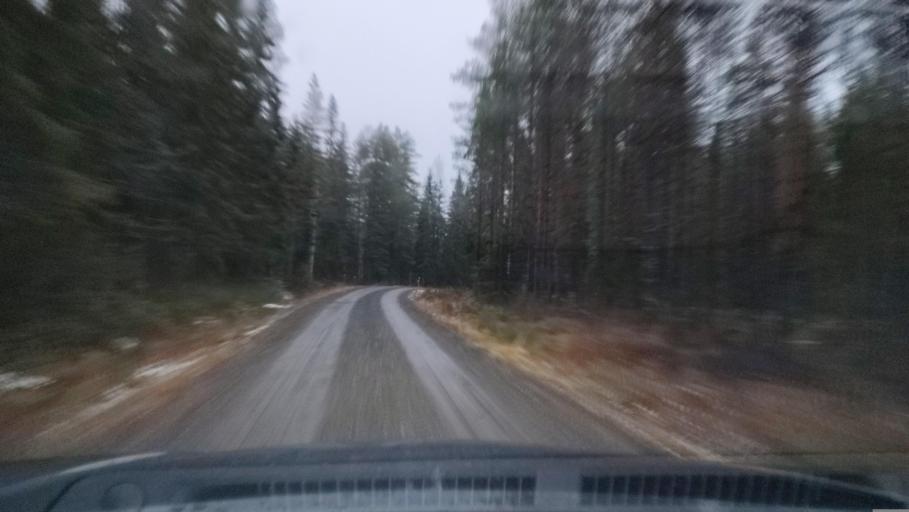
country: FI
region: Southern Ostrobothnia
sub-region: Suupohja
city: Karijoki
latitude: 62.1381
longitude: 21.6269
